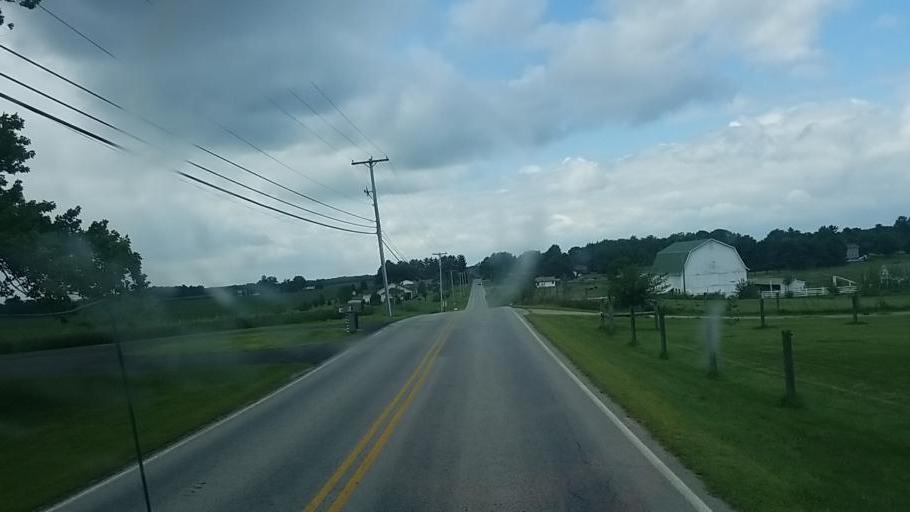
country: US
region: Ohio
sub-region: Clark County
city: Springfield
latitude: 39.8773
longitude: -83.7681
